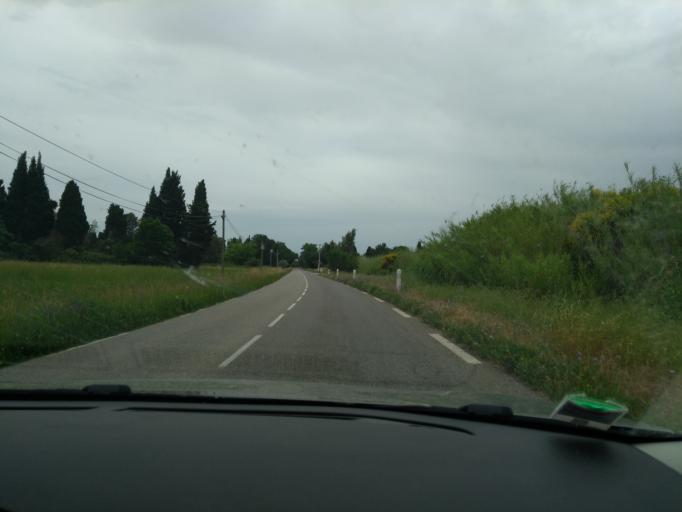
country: FR
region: Provence-Alpes-Cote d'Azur
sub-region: Departement des Bouches-du-Rhone
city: Eyguieres
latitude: 43.6479
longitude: 5.0191
